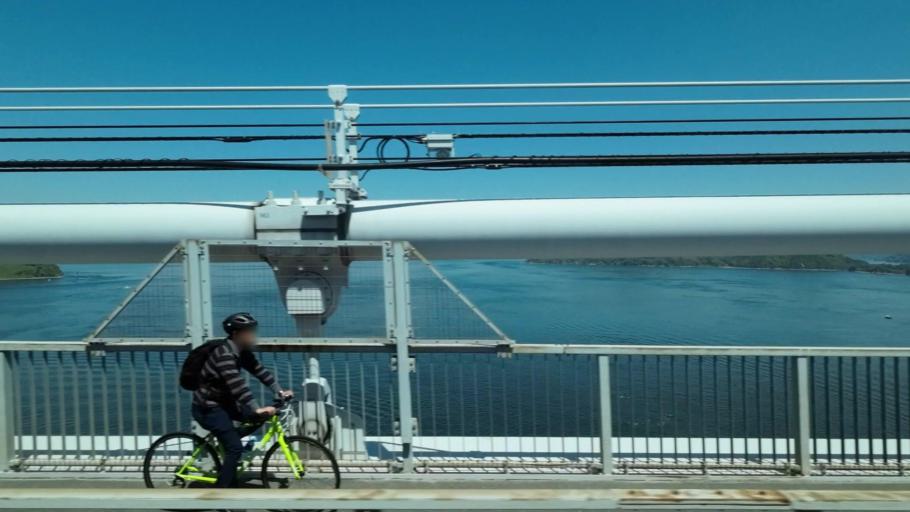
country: JP
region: Hiroshima
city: Takehara
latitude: 34.1217
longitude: 132.9995
